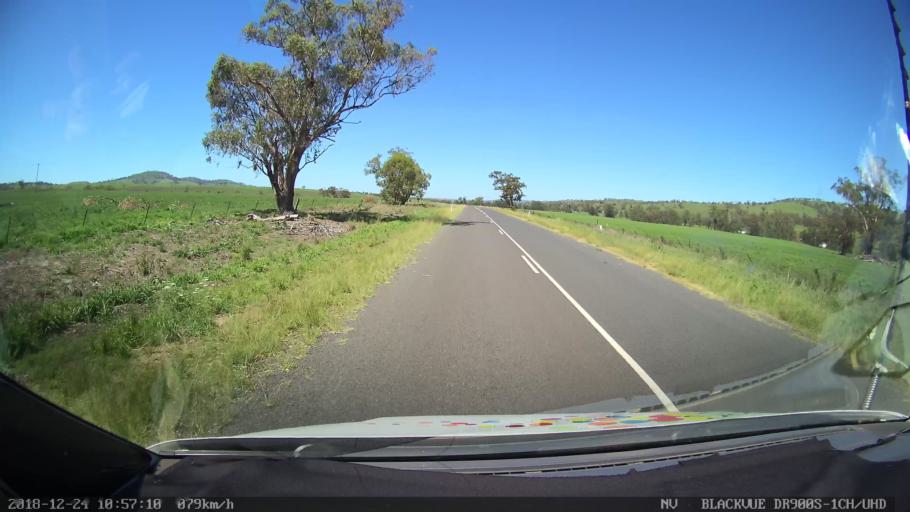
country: AU
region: New South Wales
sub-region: Upper Hunter Shire
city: Merriwa
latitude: -32.0333
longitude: 150.4152
